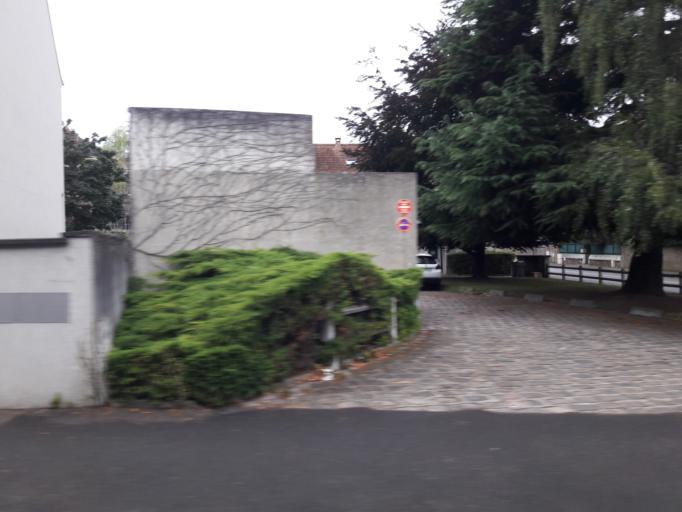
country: FR
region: Ile-de-France
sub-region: Departement de l'Essonne
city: Longjumeau
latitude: 48.6937
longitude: 2.2972
